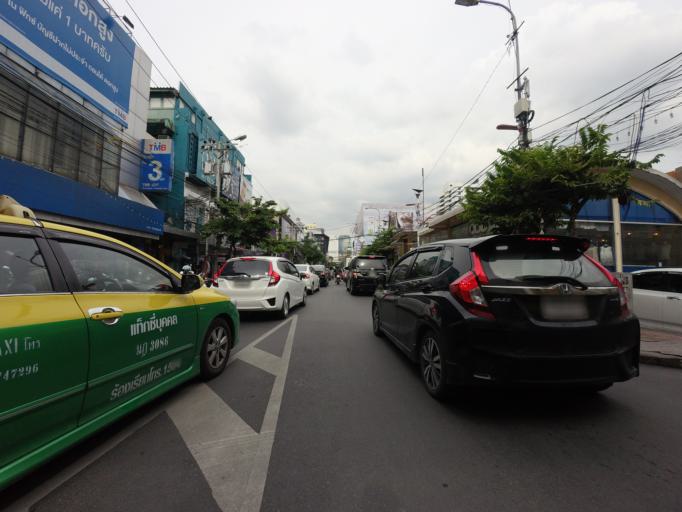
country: TH
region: Bangkok
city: Pathum Wan
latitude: 13.7448
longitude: 100.5310
